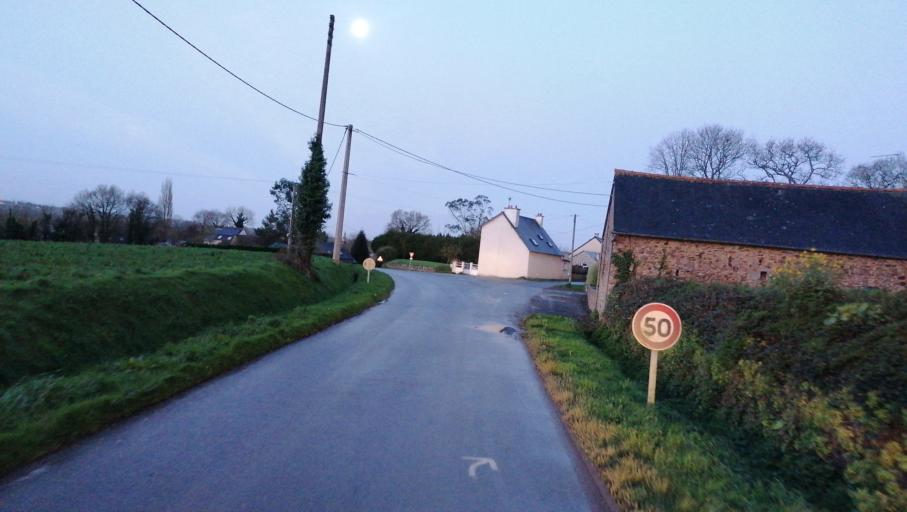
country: FR
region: Brittany
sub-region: Departement des Cotes-d'Armor
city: Lanvollon
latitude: 48.6704
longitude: -2.9724
